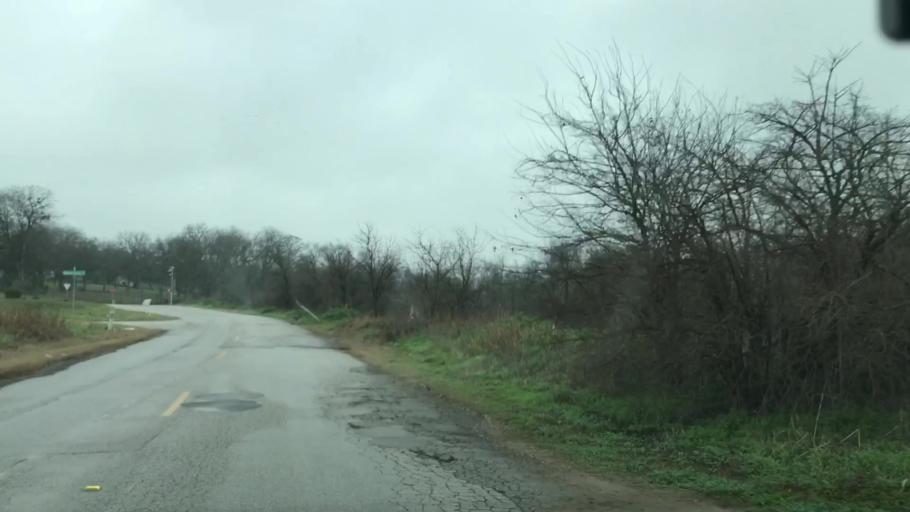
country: US
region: Texas
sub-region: Hays County
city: San Marcos
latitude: 29.8931
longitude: -97.9004
